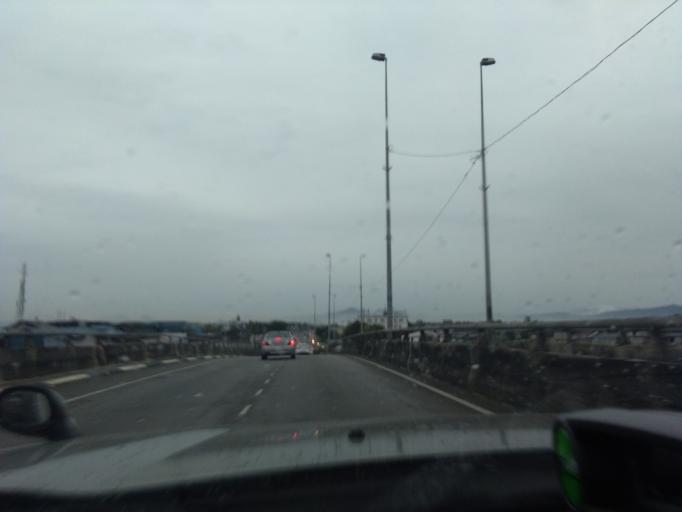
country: MY
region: Penang
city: Nibong Tebal
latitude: 5.1725
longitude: 100.4799
